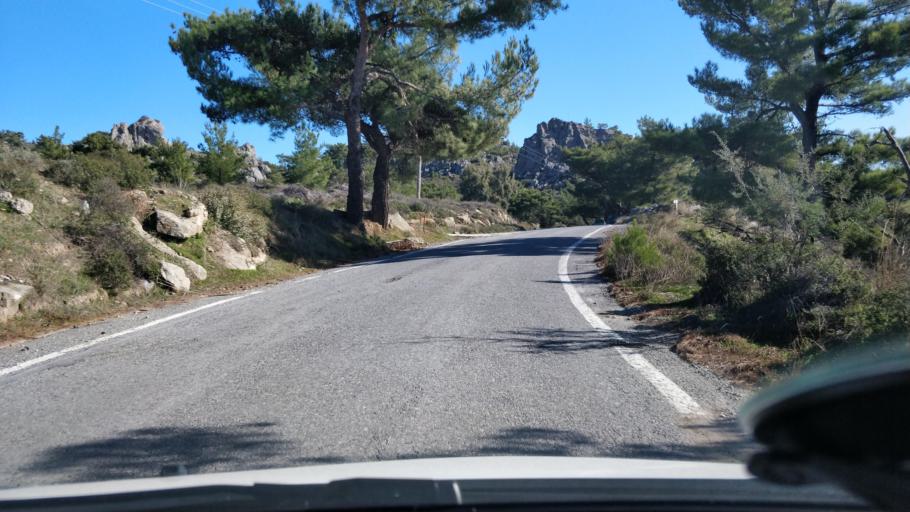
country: GR
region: Crete
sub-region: Nomos Lasithiou
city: Gra Liyia
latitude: 35.0452
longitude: 25.6360
